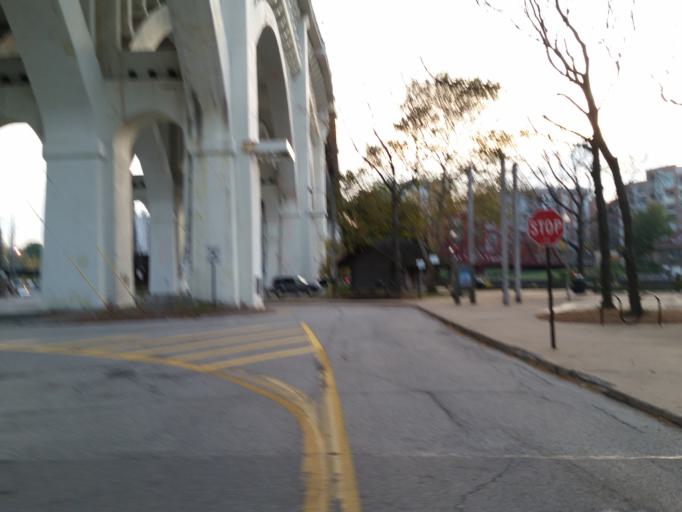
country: US
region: Ohio
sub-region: Cuyahoga County
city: Cleveland
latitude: 41.4952
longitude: -81.7016
